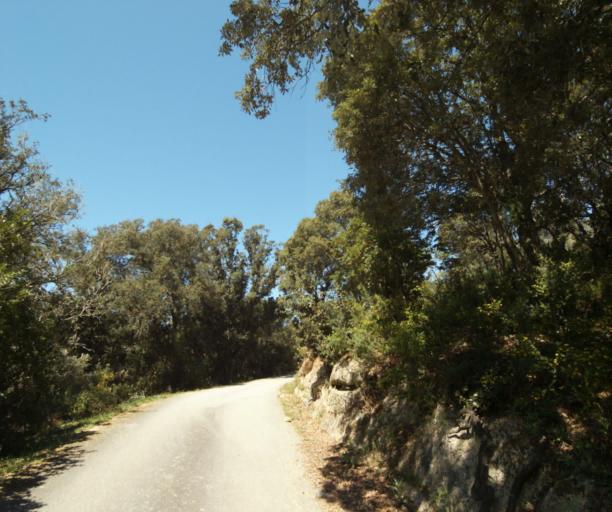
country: FR
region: Corsica
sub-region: Departement de la Corse-du-Sud
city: Propriano
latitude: 41.6394
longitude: 8.8690
